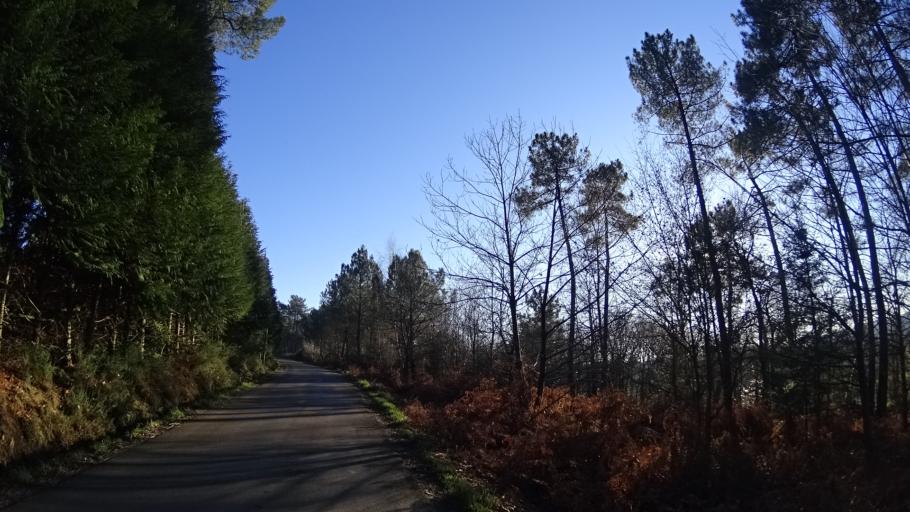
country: FR
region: Brittany
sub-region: Departement du Morbihan
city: Allaire
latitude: 47.6627
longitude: -2.1794
